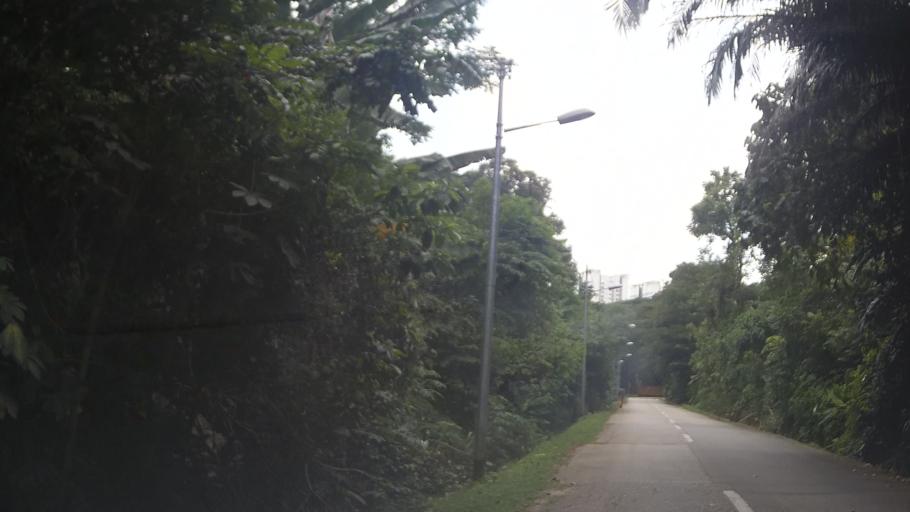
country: MY
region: Johor
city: Kampung Pasir Gudang Baru
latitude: 1.3980
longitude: 103.8706
